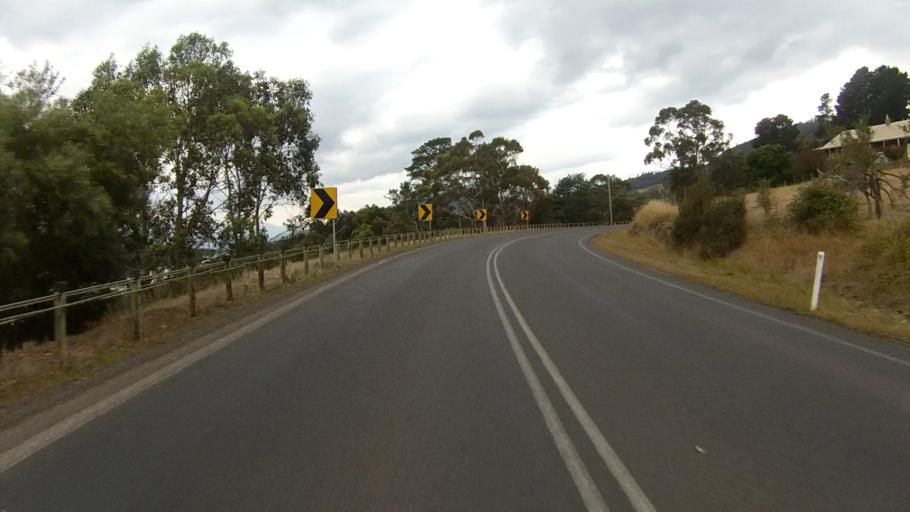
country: AU
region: Tasmania
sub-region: Huon Valley
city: Franklin
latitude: -43.0900
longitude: 147.0242
